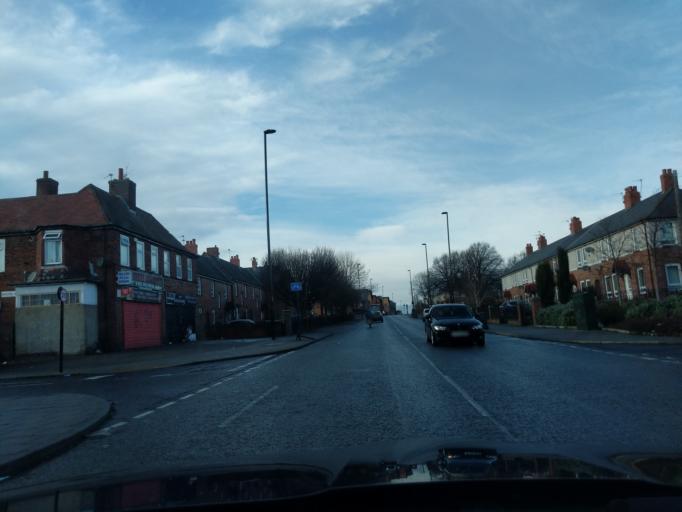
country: GB
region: England
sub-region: Gateshead
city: Felling
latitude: 54.9651
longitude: -1.5590
